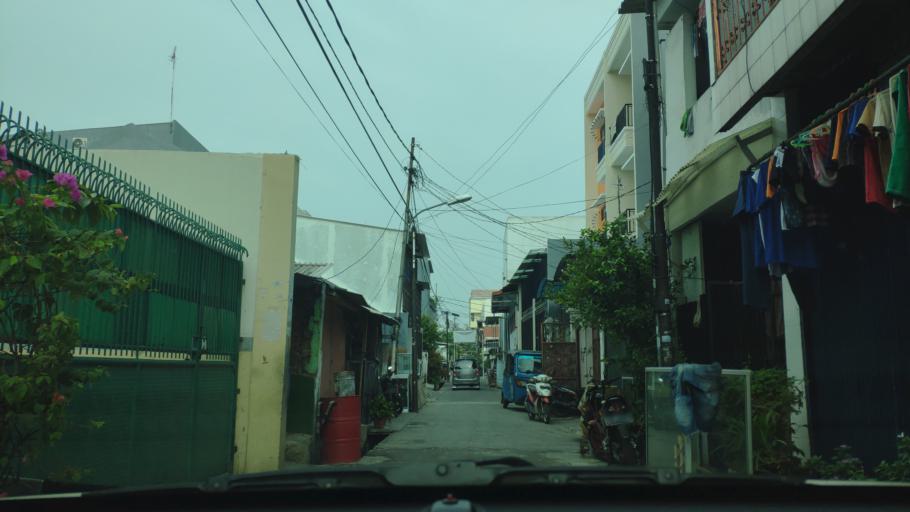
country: ID
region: Jakarta Raya
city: Jakarta
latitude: -6.1587
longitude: 106.8136
